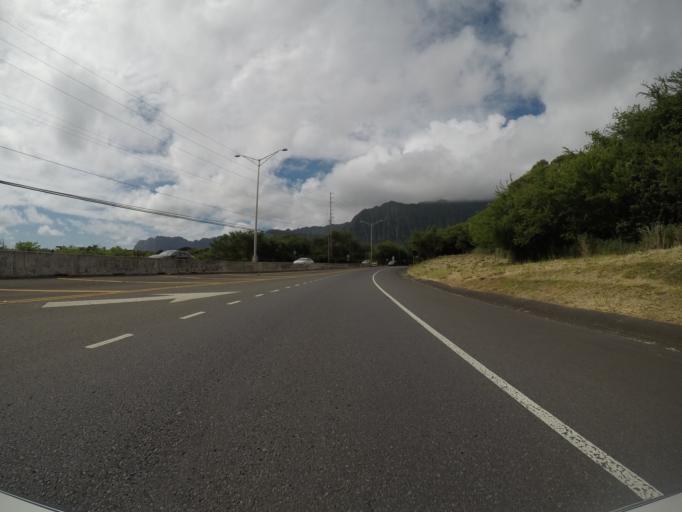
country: US
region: Hawaii
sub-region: Honolulu County
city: Waimanalo
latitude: 21.3543
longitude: -157.7297
